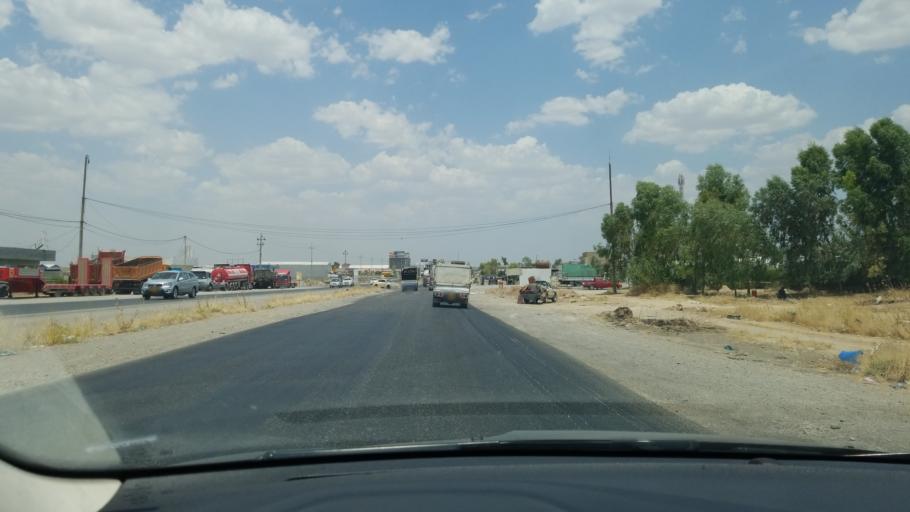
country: IQ
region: Arbil
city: Erbil
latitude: 36.0953
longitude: 44.0218
